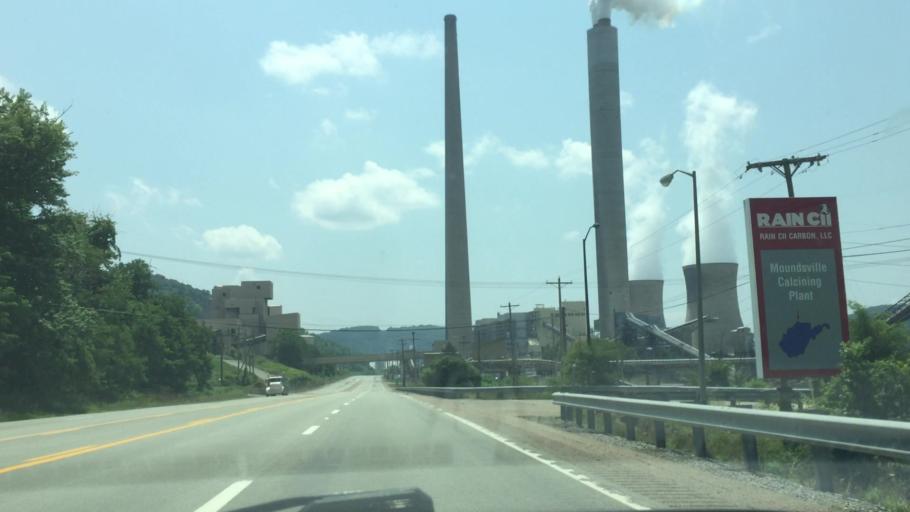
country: US
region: Ohio
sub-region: Belmont County
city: Powhatan Point
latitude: 39.8380
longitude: -80.8158
